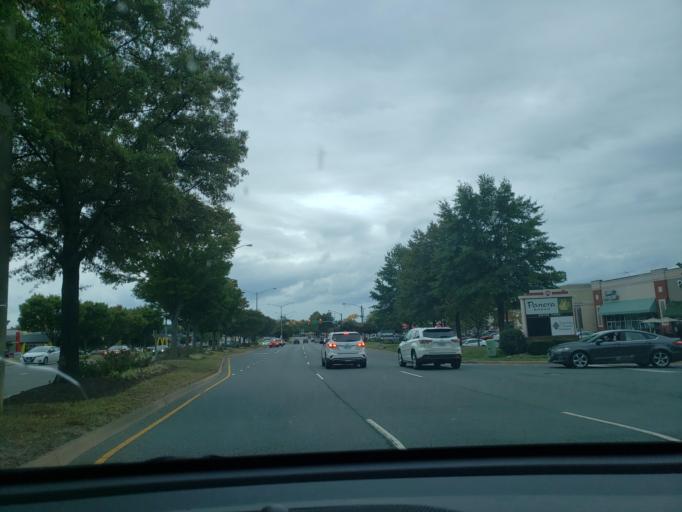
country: US
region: Virginia
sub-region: Stafford County
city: Falmouth
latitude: 38.3062
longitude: -77.5103
